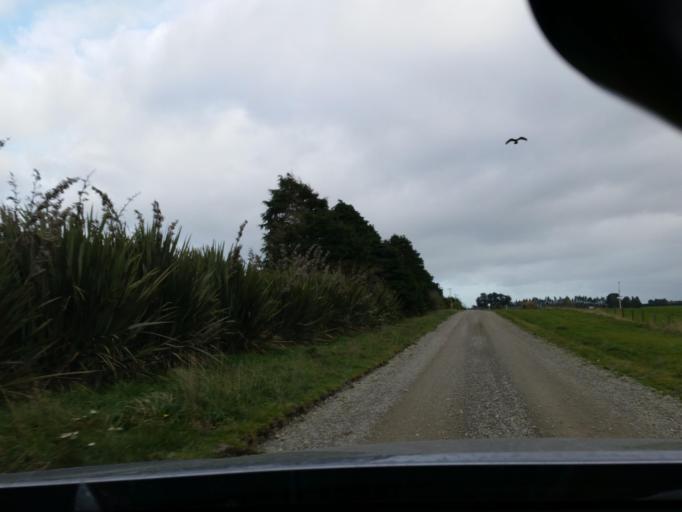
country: NZ
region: Southland
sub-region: Southland District
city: Winton
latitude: -46.2639
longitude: 168.3673
